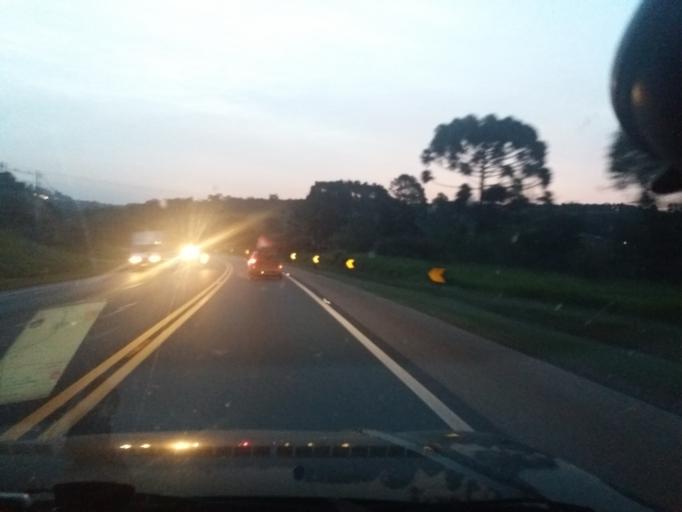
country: BR
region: Sao Paulo
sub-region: Itapeva
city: Itapeva
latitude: -23.9763
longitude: -48.8391
